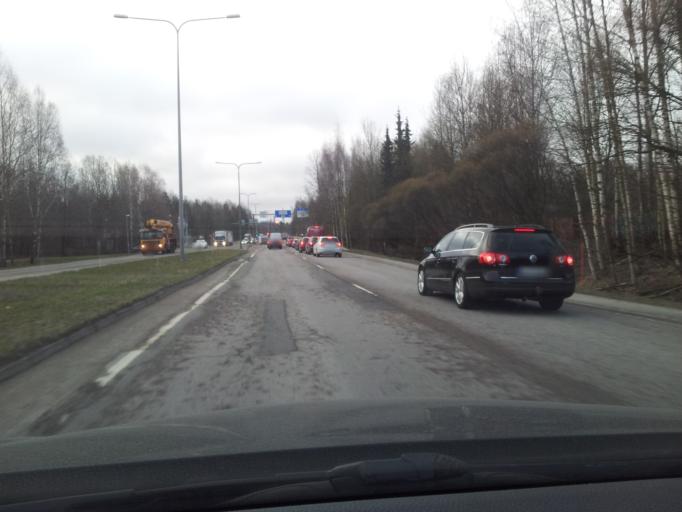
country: FI
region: Uusimaa
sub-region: Helsinki
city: Teekkarikylae
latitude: 60.2287
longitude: 24.8708
